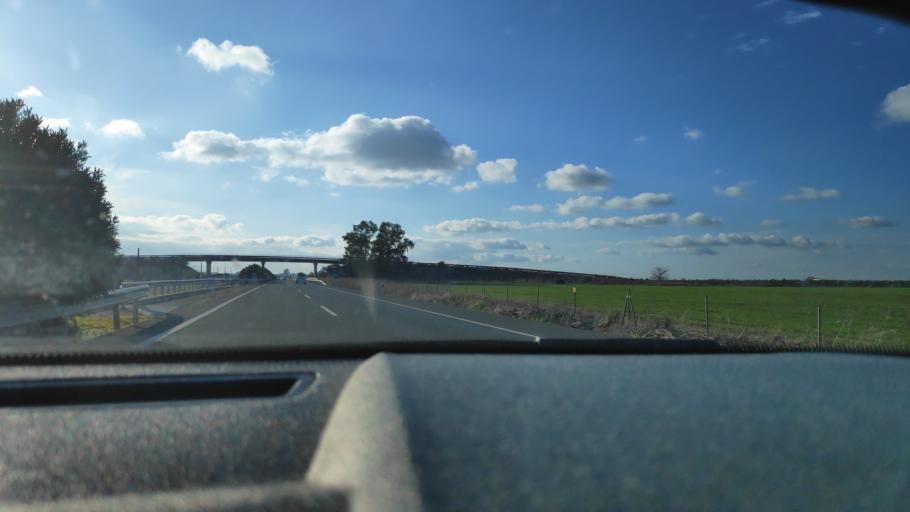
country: ES
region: Andalusia
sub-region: Provincia de Sevilla
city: Fuentes de Andalucia
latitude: 37.5139
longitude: -5.3333
